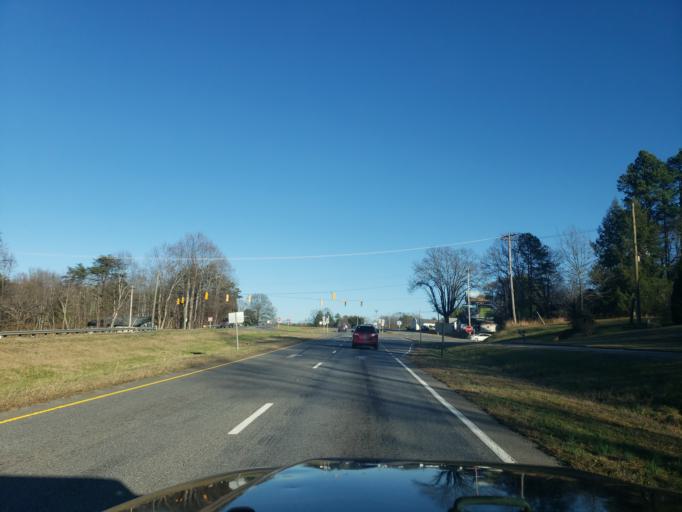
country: US
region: North Carolina
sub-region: Gaston County
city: Bessemer City
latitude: 35.2485
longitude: -81.2879
